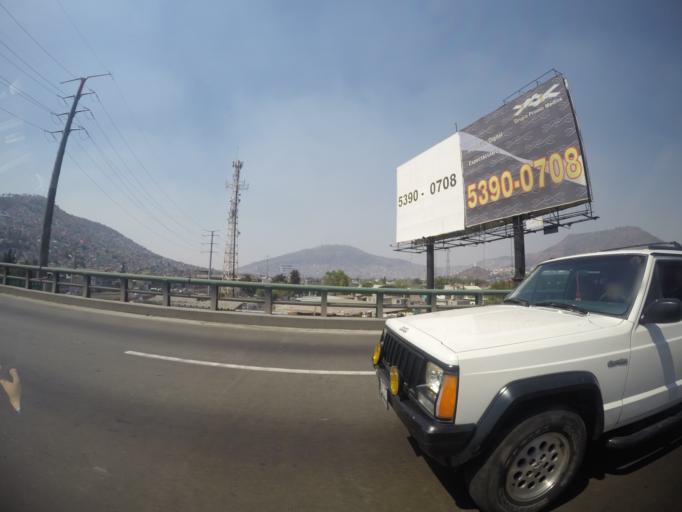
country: MX
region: Mexico City
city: Gustavo A. Madero
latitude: 19.5154
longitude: -99.1009
